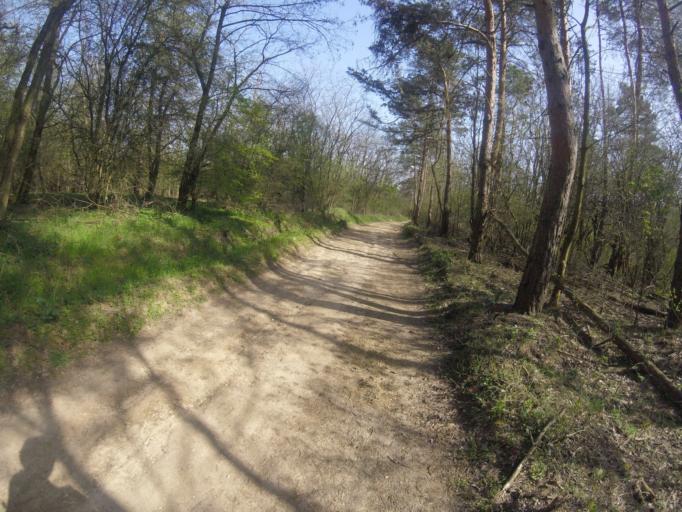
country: HU
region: Pest
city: Pilisszentivan
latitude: 47.6336
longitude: 18.8798
